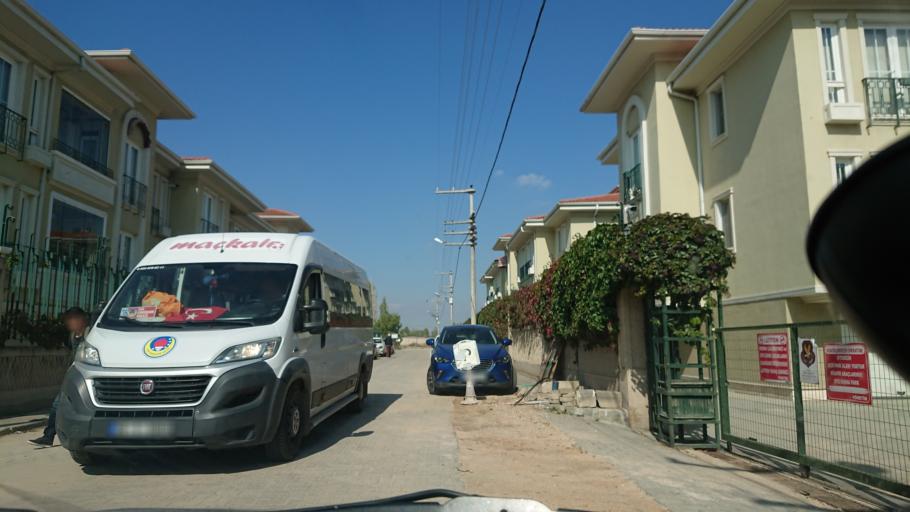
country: TR
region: Eskisehir
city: Eskisehir
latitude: 39.7550
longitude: 30.4783
